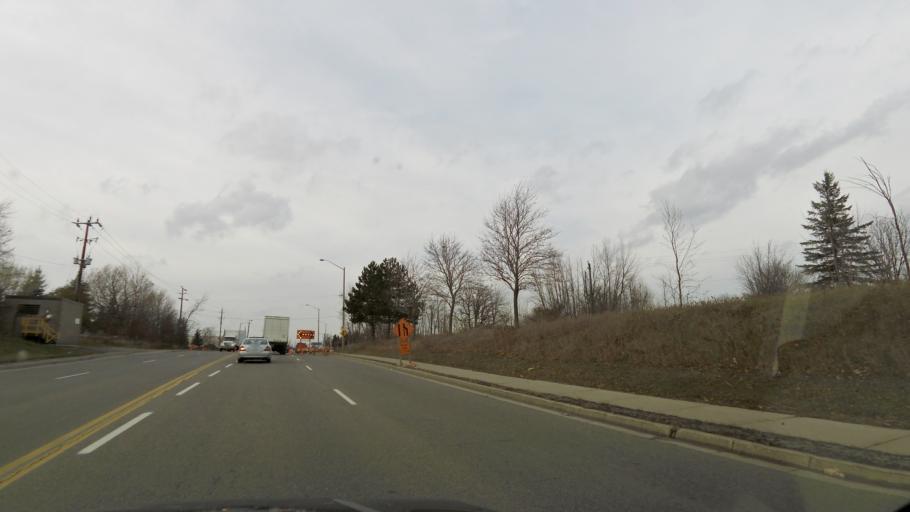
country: CA
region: Ontario
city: Etobicoke
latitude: 43.7383
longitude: -79.6409
